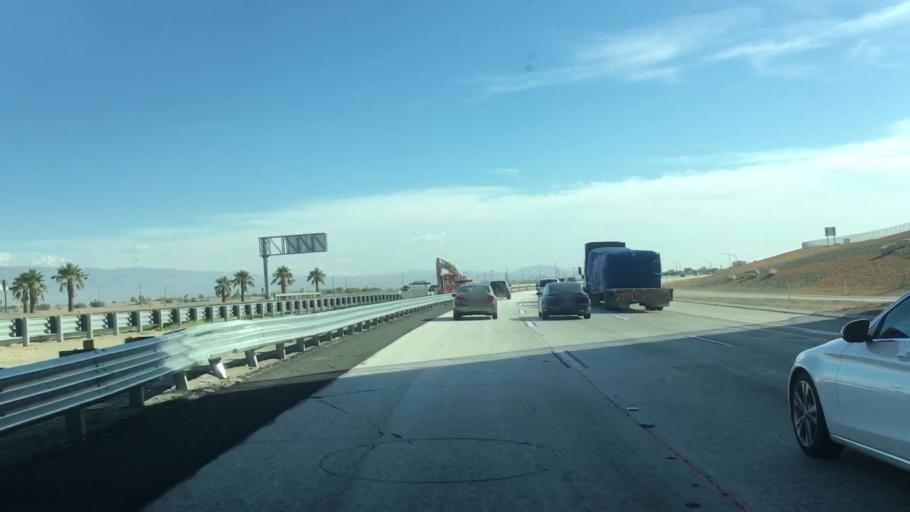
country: US
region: California
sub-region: Riverside County
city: Bermuda Dunes
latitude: 33.7493
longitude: -116.2685
